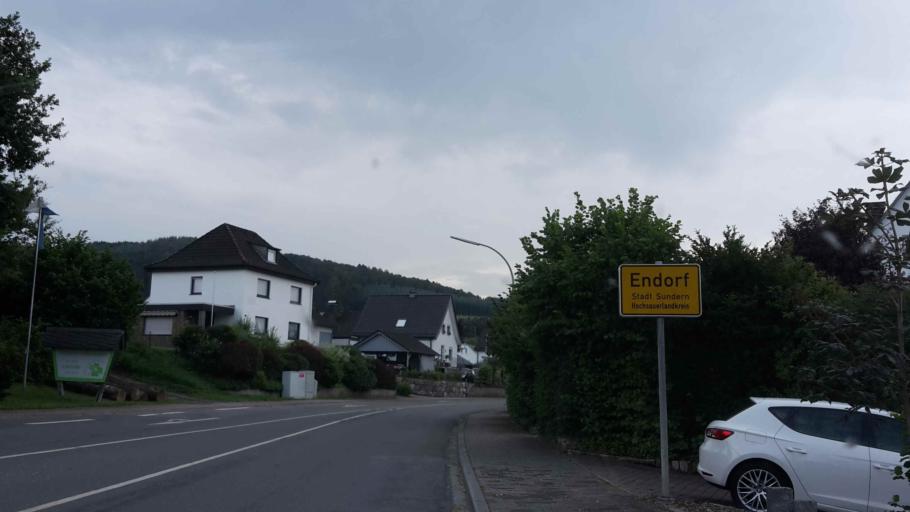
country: DE
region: North Rhine-Westphalia
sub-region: Regierungsbezirk Arnsberg
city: Sundern
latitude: 51.2934
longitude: 8.0435
